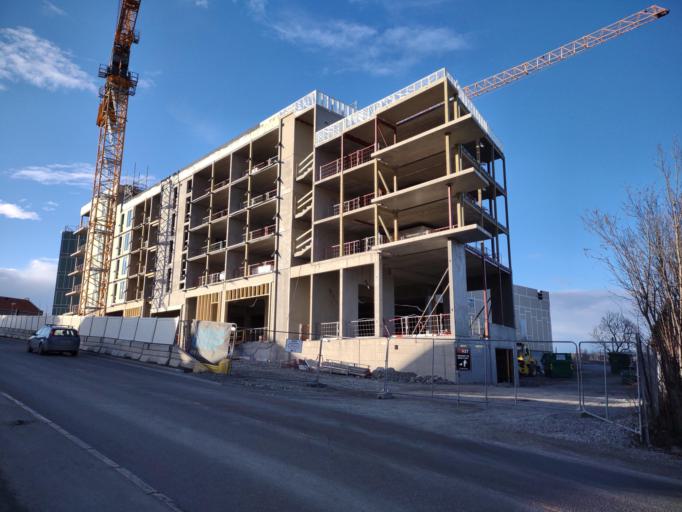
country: NO
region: Akershus
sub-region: Skedsmo
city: Lillestrom
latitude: 59.9615
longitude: 11.0107
